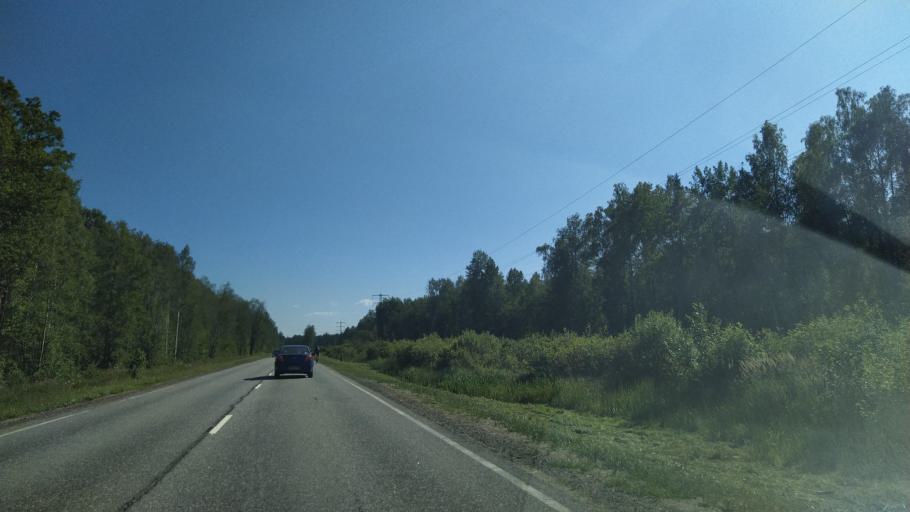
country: RU
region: Leningrad
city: Imeni Morozova
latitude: 60.0203
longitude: 31.0367
